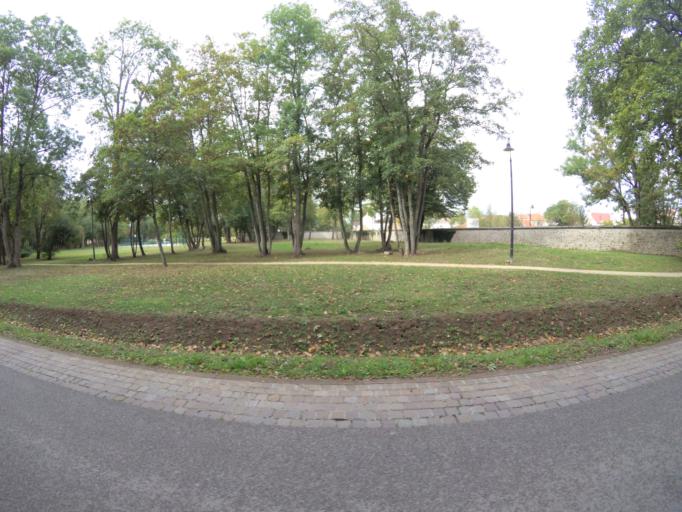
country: FR
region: Ile-de-France
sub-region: Departement de Seine-et-Marne
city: Chessy
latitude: 48.8762
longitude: 2.7699
